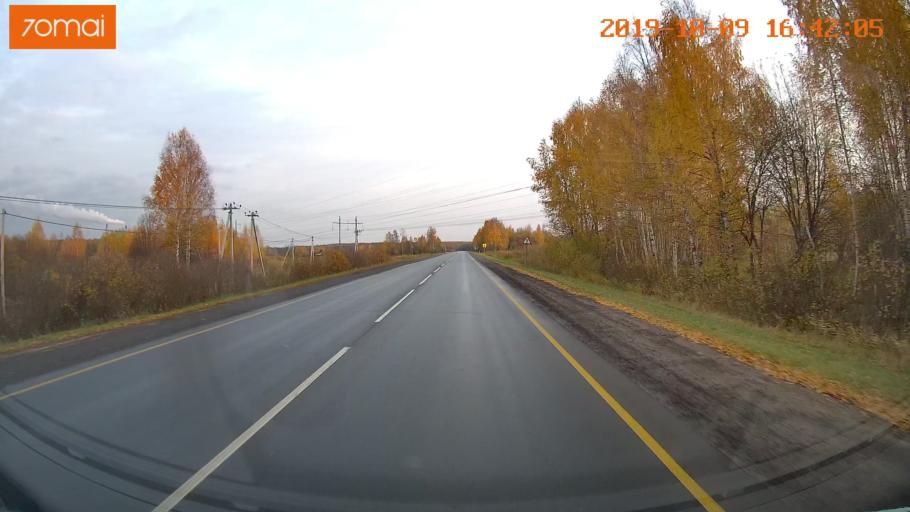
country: RU
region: Kostroma
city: Volgorechensk
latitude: 57.4660
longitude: 41.0935
